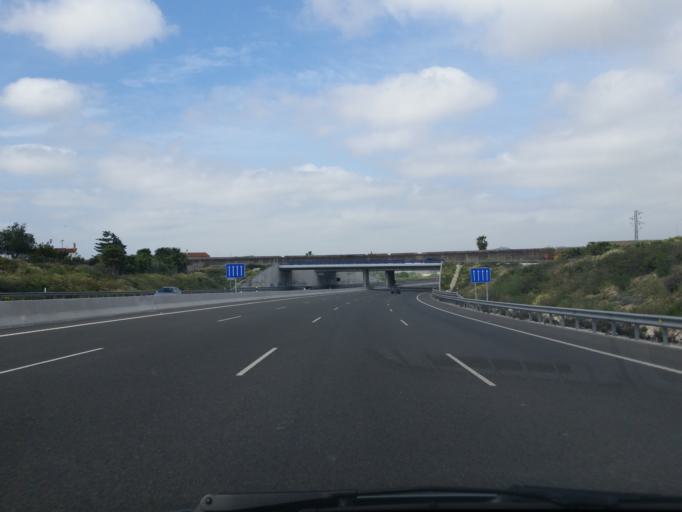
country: ES
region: Andalusia
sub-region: Provincia de Malaga
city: Alhaurin de la Torre
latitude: 36.6852
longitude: -4.5267
